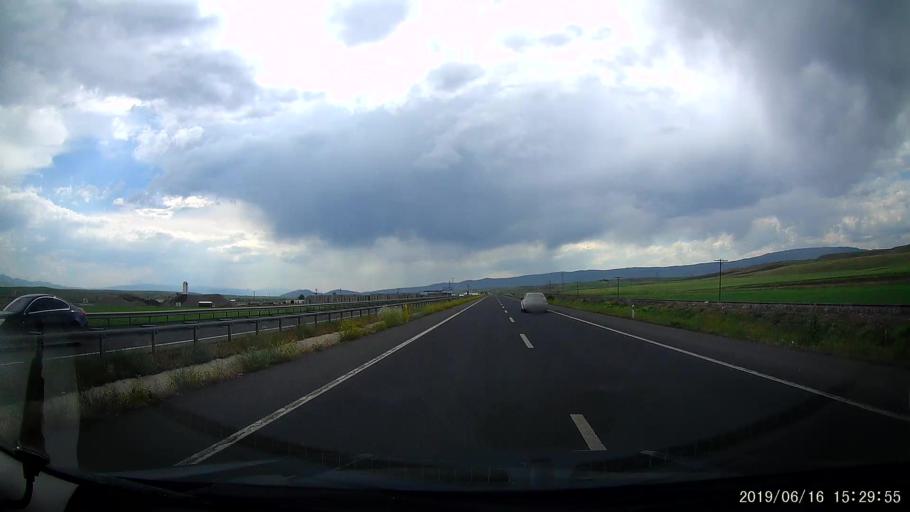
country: TR
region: Erzurum
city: Horasan
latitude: 40.0327
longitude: 42.1198
